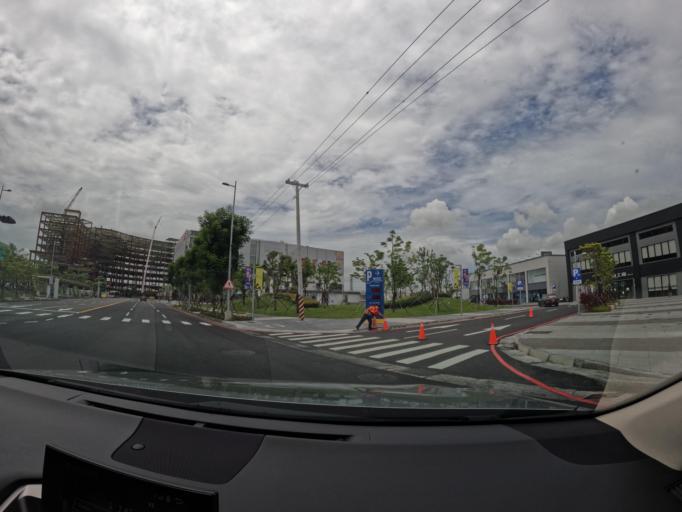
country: TW
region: Kaohsiung
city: Kaohsiung
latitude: 22.7812
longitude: 120.3002
